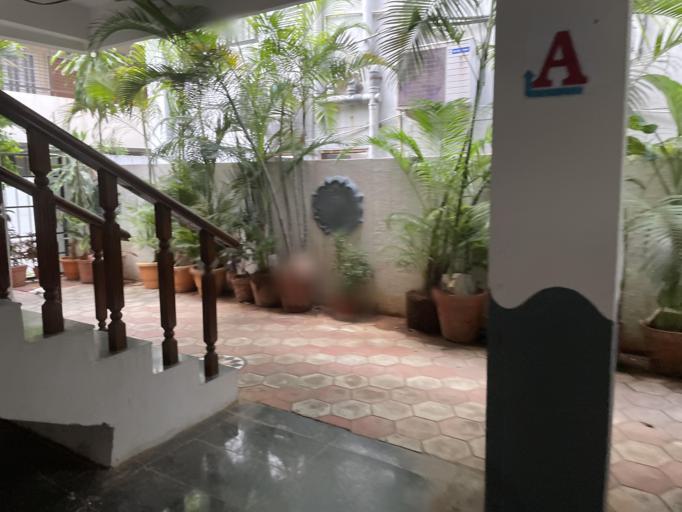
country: IN
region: Telangana
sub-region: Hyderabad
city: Hyderabad
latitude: 17.4274
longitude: 78.4556
